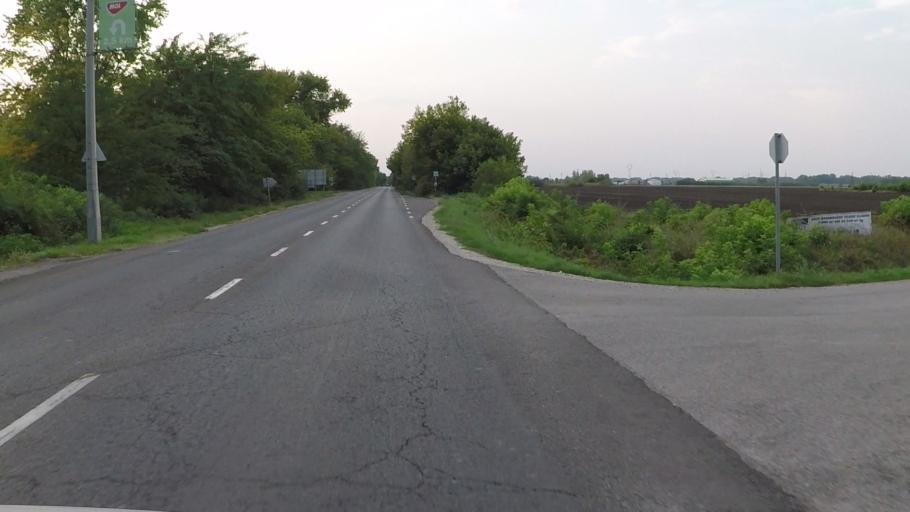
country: HU
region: Jasz-Nagykun-Szolnok
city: Szolnok
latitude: 47.1936
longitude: 20.1713
